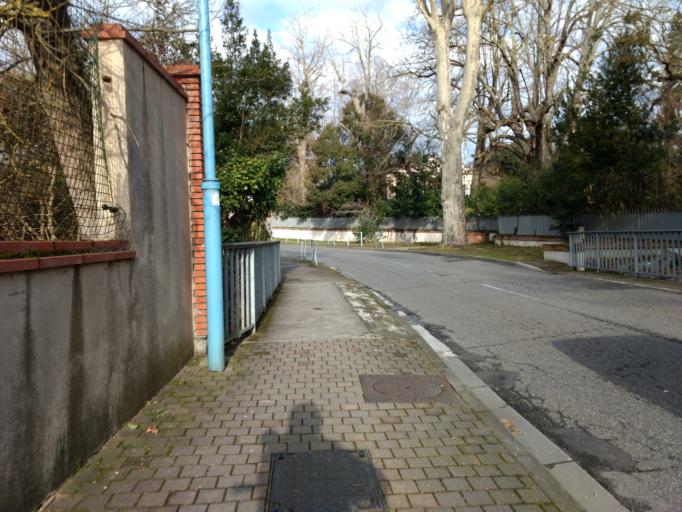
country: FR
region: Midi-Pyrenees
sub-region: Departement de la Haute-Garonne
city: Tournefeuille
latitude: 43.5827
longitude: 1.3493
